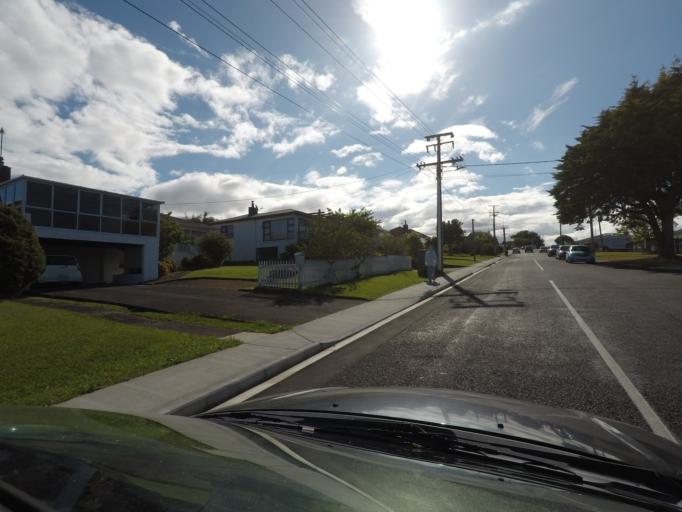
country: NZ
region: Auckland
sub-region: Auckland
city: Rosebank
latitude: -36.8655
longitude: 174.6487
